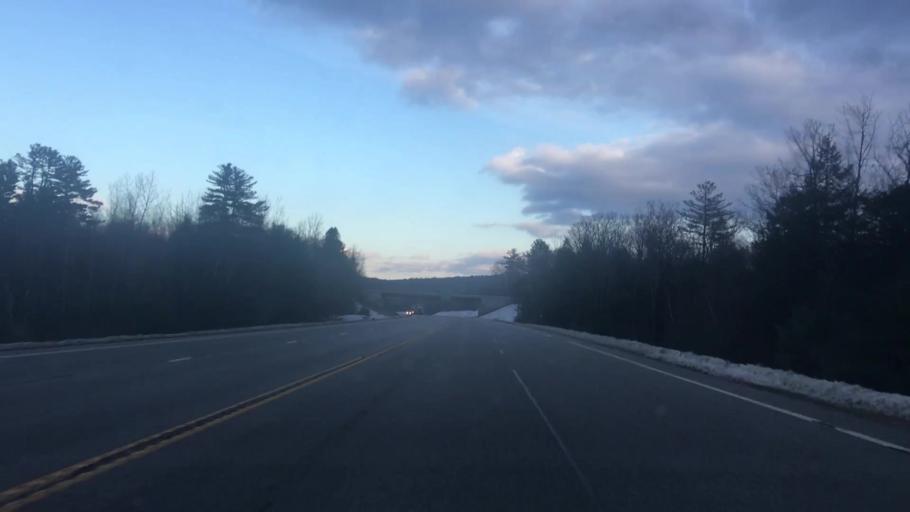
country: US
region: New Hampshire
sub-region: Hillsborough County
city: Hillsborough
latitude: 43.1203
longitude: -71.9045
